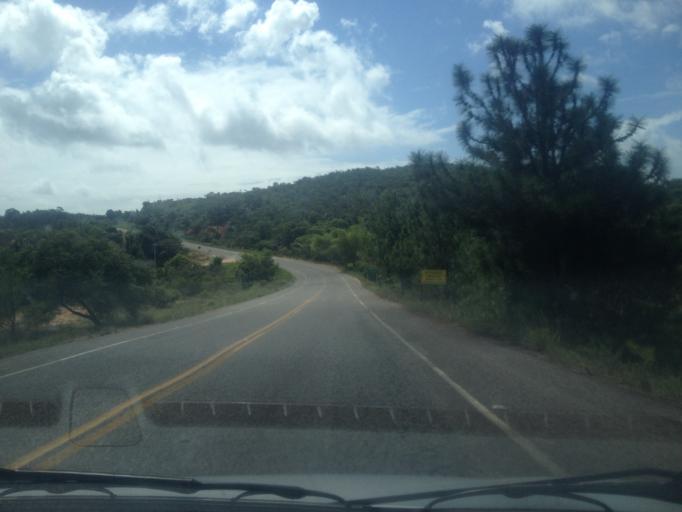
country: BR
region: Bahia
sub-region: Conde
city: Conde
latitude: -11.9798
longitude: -37.6757
